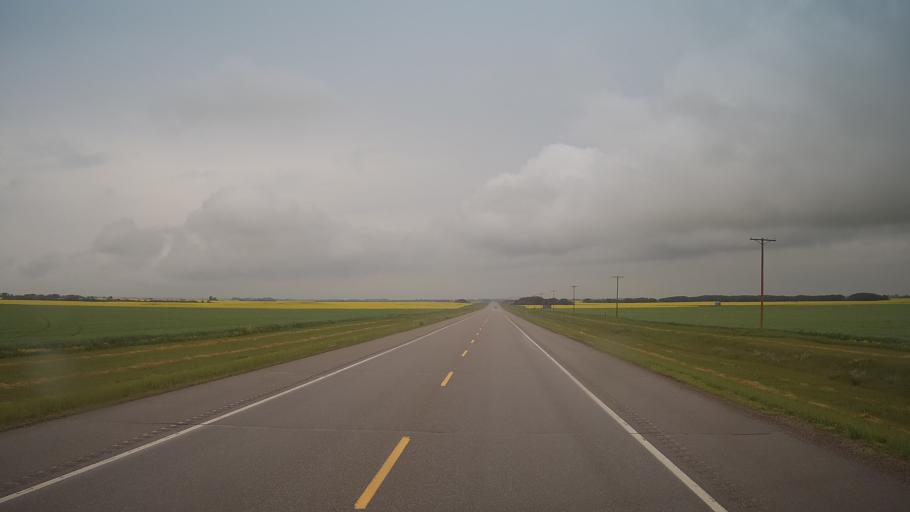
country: CA
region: Saskatchewan
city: Wilkie
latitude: 52.4219
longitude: -108.8989
